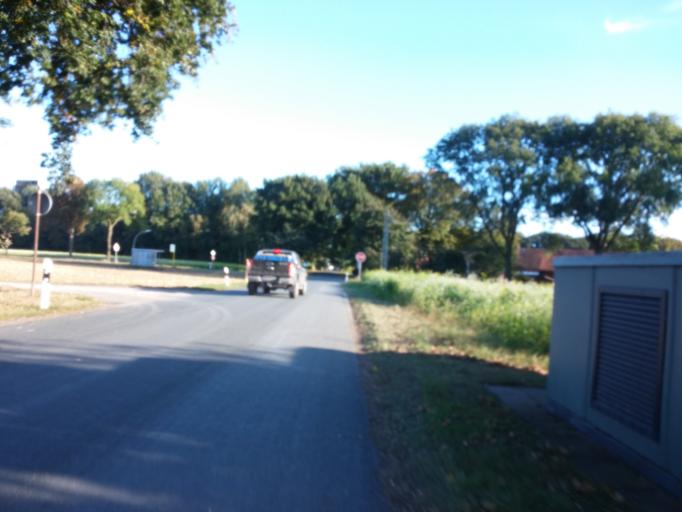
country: DE
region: North Rhine-Westphalia
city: Dorsten
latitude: 51.6402
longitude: 7.0153
